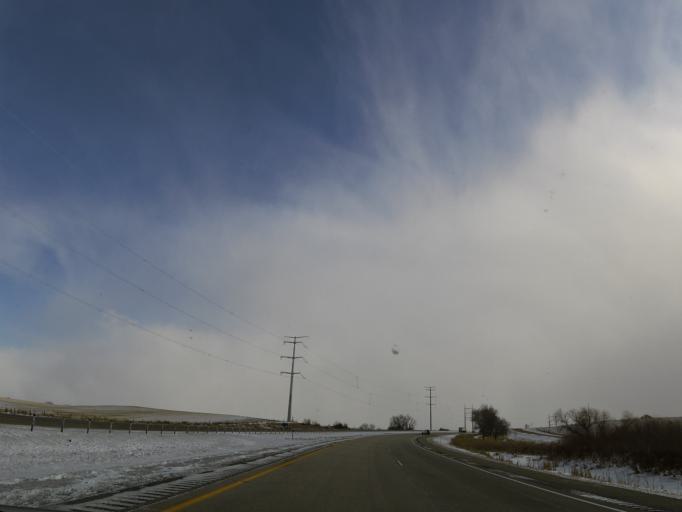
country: US
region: Minnesota
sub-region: Grant County
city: Elbow Lake
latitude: 46.1062
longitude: -95.8950
